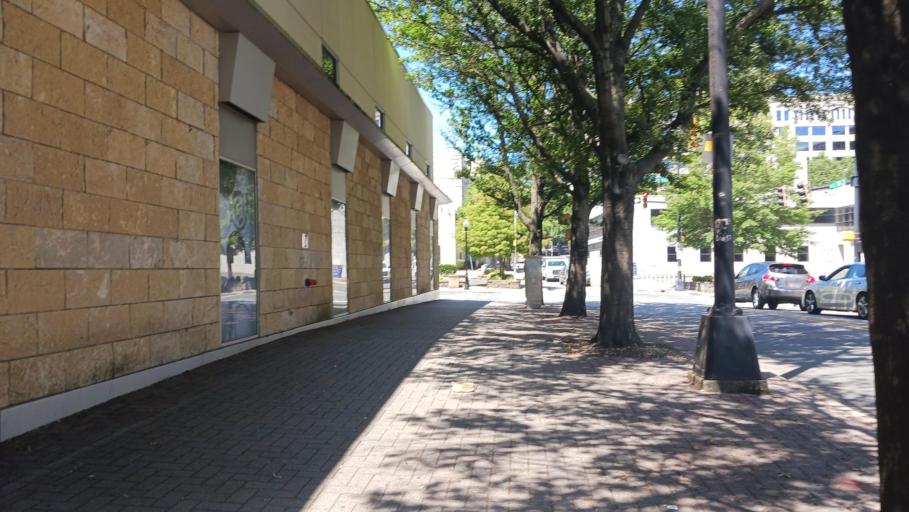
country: US
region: North Carolina
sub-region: Mecklenburg County
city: Charlotte
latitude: 35.2283
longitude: -80.8384
